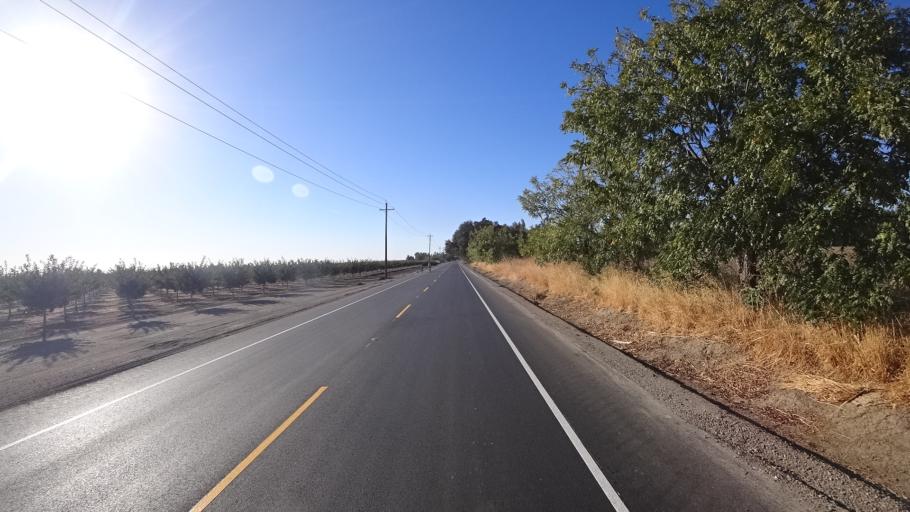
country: US
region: California
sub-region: Yolo County
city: Woodland
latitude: 38.6378
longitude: -121.7847
